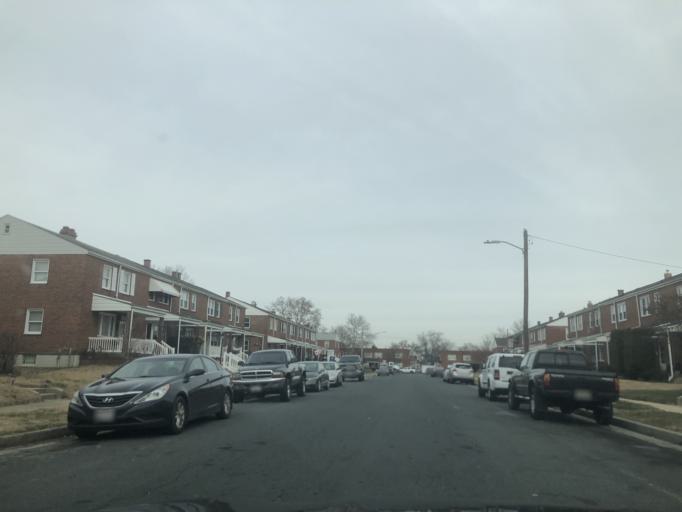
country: US
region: Maryland
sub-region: Baltimore County
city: Dundalk
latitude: 39.2674
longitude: -76.4905
